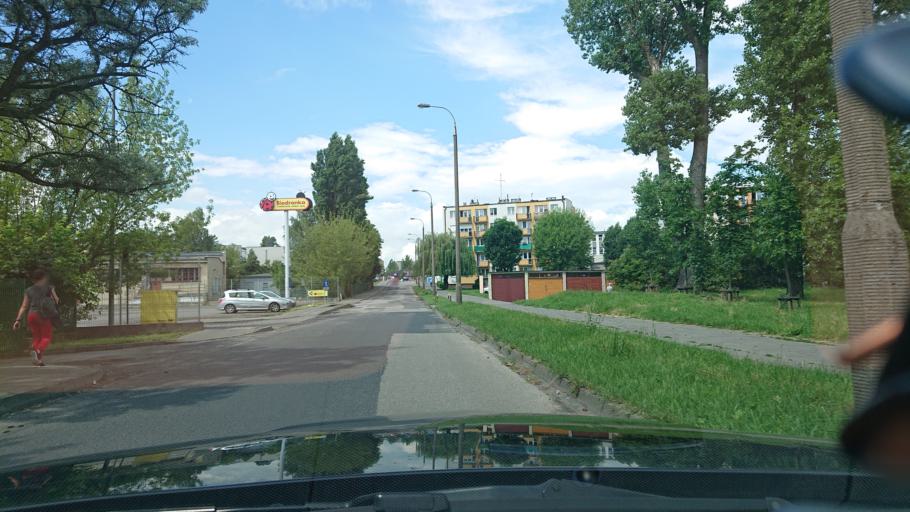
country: PL
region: Greater Poland Voivodeship
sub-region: Powiat gnieznienski
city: Gniezno
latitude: 52.5407
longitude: 17.6113
